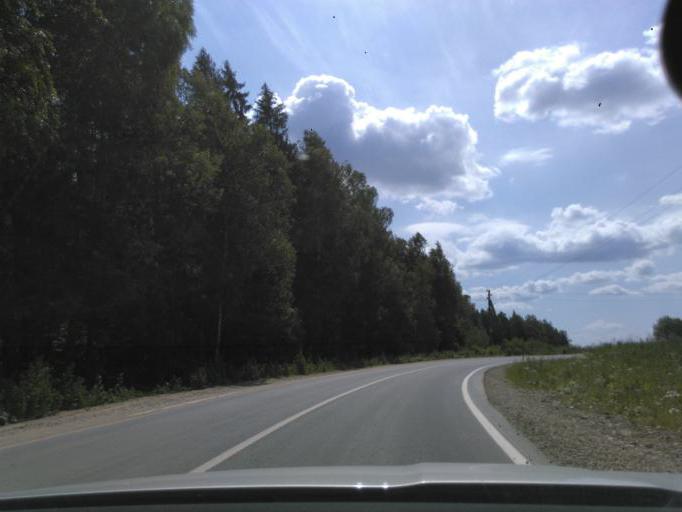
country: RU
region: Moskovskaya
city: Solnechnogorsk
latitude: 56.1390
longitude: 36.9767
